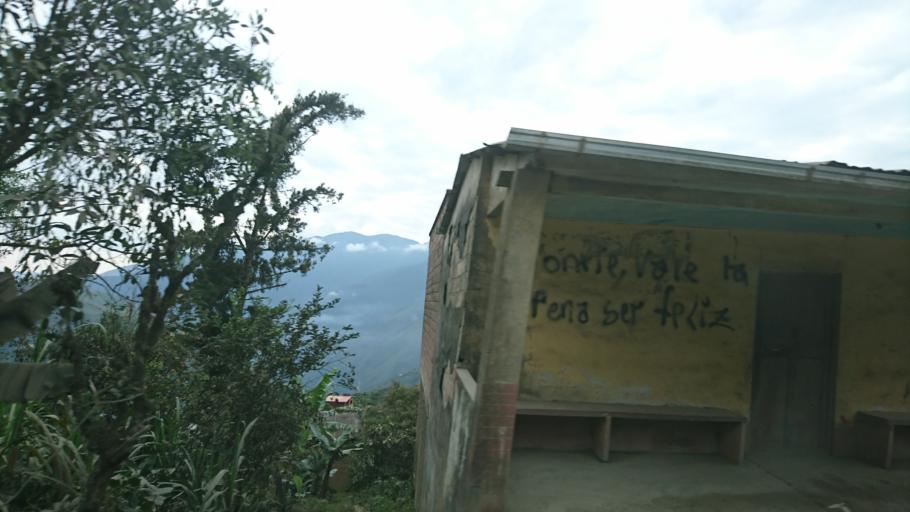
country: BO
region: La Paz
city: Coroico
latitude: -16.1988
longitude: -67.7031
